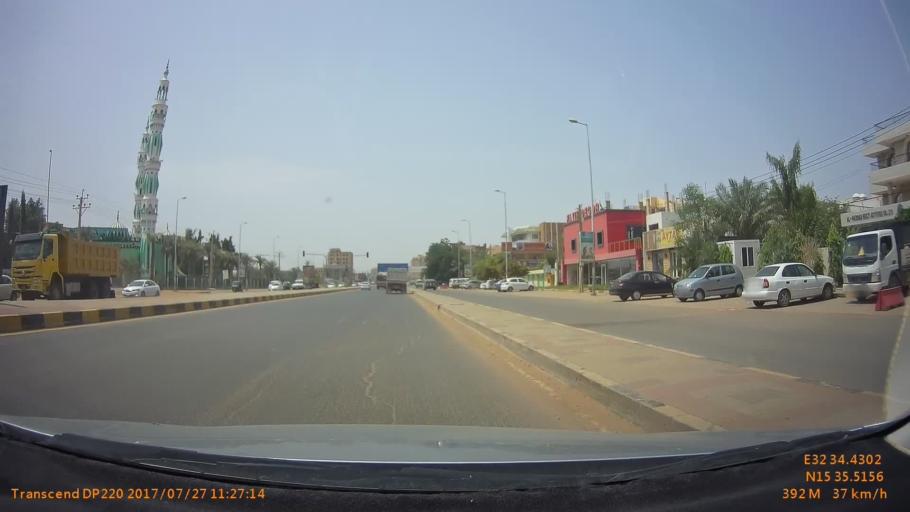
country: SD
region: Khartoum
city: Khartoum
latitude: 15.5918
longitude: 32.5738
